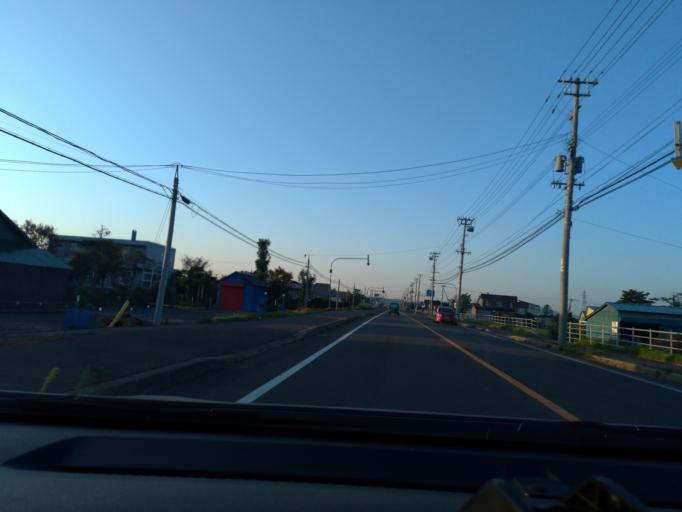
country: JP
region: Hokkaido
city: Tobetsu
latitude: 43.2008
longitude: 141.5217
